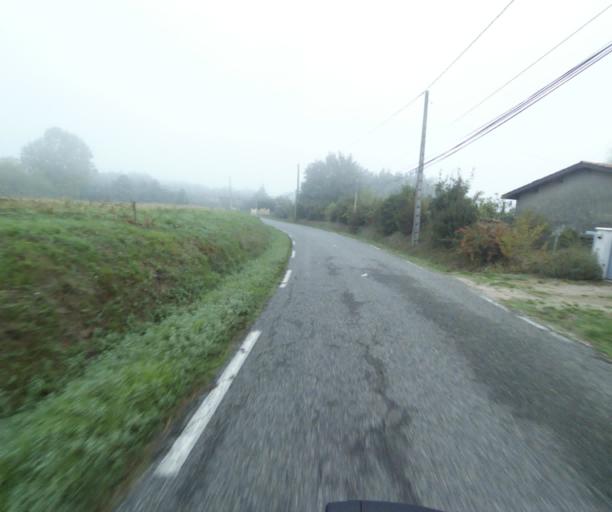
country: FR
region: Midi-Pyrenees
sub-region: Departement du Tarn-et-Garonne
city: Corbarieu
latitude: 43.9533
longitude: 1.3960
